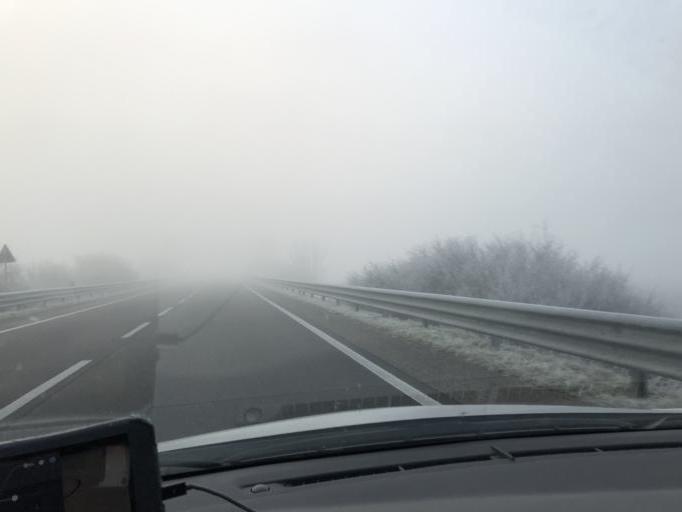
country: IT
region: Latium
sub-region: Provincia di Rieti
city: Limiti di Greccio
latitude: 42.4724
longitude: 12.7759
